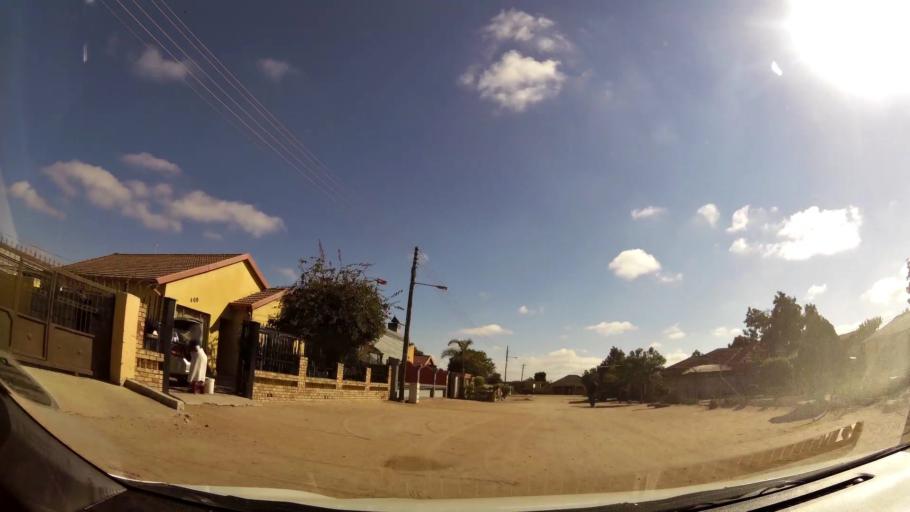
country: ZA
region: Limpopo
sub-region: Capricorn District Municipality
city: Polokwane
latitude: -23.8660
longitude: 29.3868
